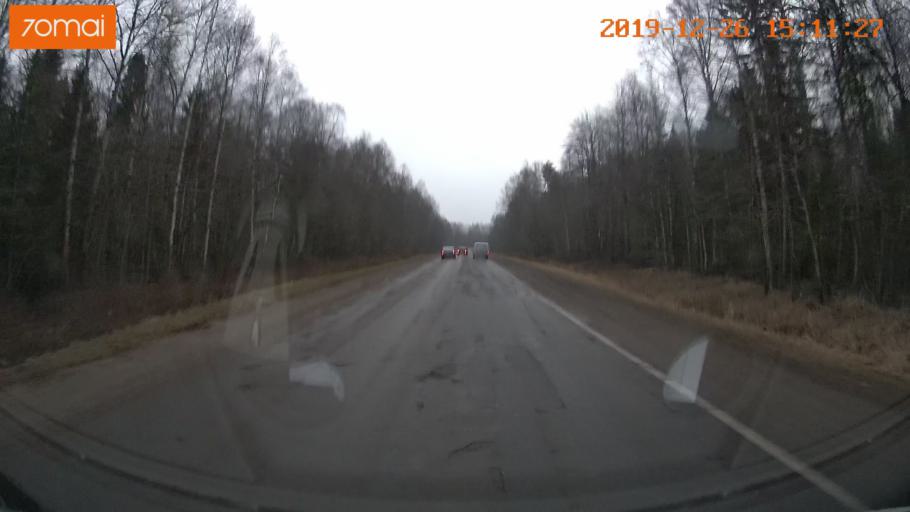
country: RU
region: Jaroslavl
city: Rybinsk
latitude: 58.1344
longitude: 38.8620
